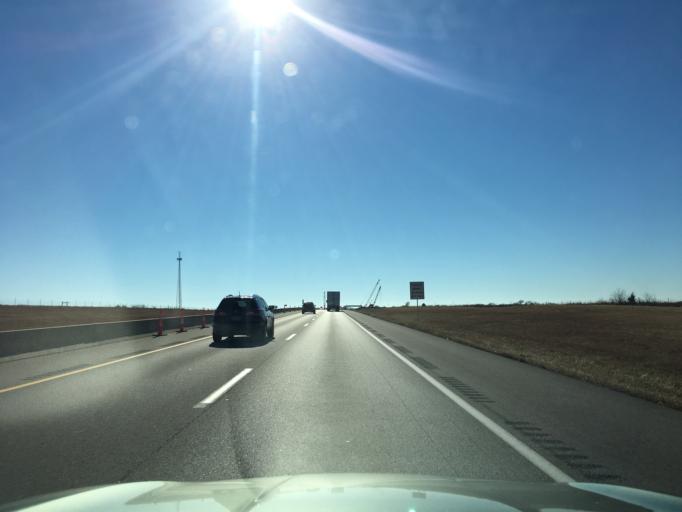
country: US
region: Kansas
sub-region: Sumner County
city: Wellington
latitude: 37.2526
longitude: -97.3390
